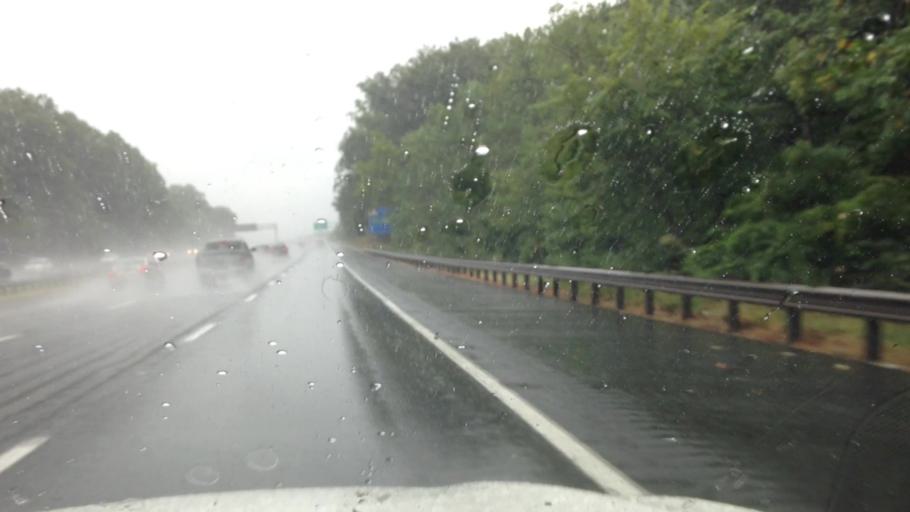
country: US
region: Maryland
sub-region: Anne Arundel County
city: Crofton
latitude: 38.9557
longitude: -76.6861
